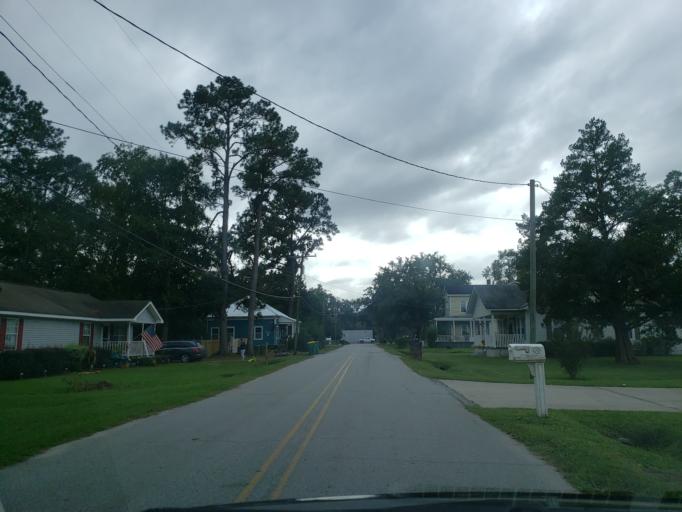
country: US
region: Georgia
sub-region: Chatham County
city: Pooler
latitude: 32.1172
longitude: -81.2465
